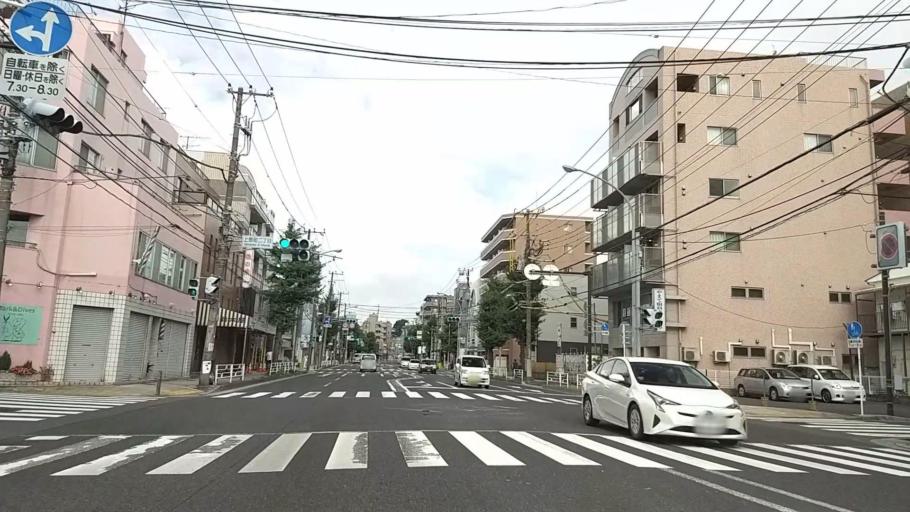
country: JP
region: Kanagawa
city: Yokohama
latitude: 35.4324
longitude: 139.6536
